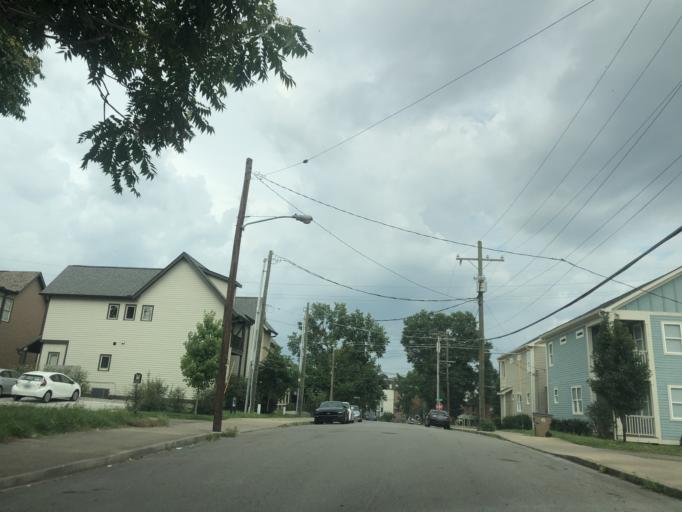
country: US
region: Tennessee
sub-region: Davidson County
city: Nashville
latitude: 36.1763
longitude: -86.7971
